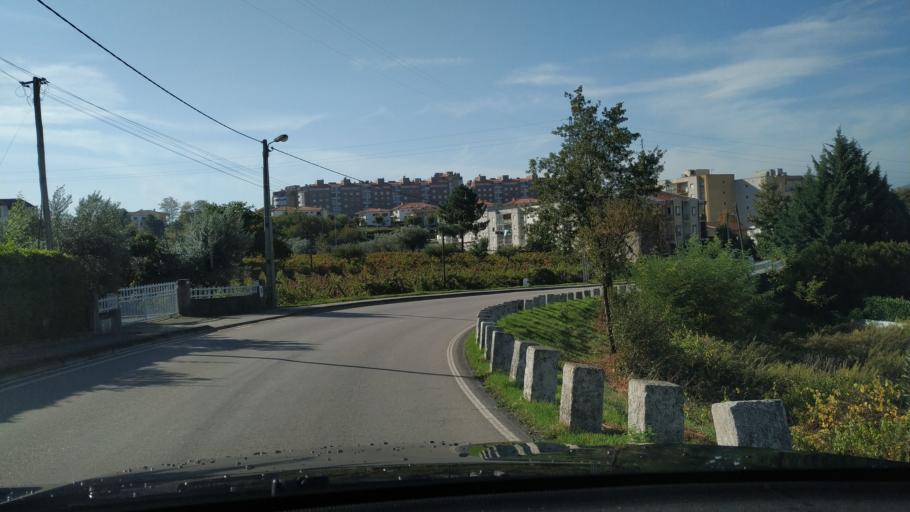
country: PT
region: Vila Real
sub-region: Vila Real
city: Vila Real
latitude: 41.3100
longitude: -7.7206
